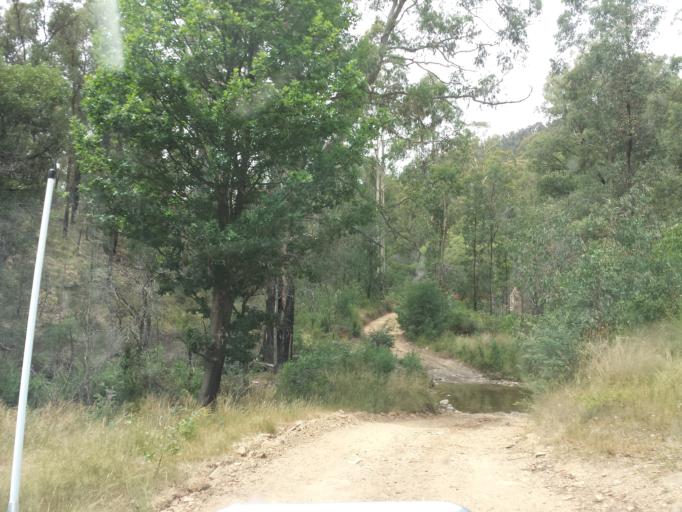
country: AU
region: Victoria
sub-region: Wellington
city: Heyfield
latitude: -37.7544
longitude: 146.5016
